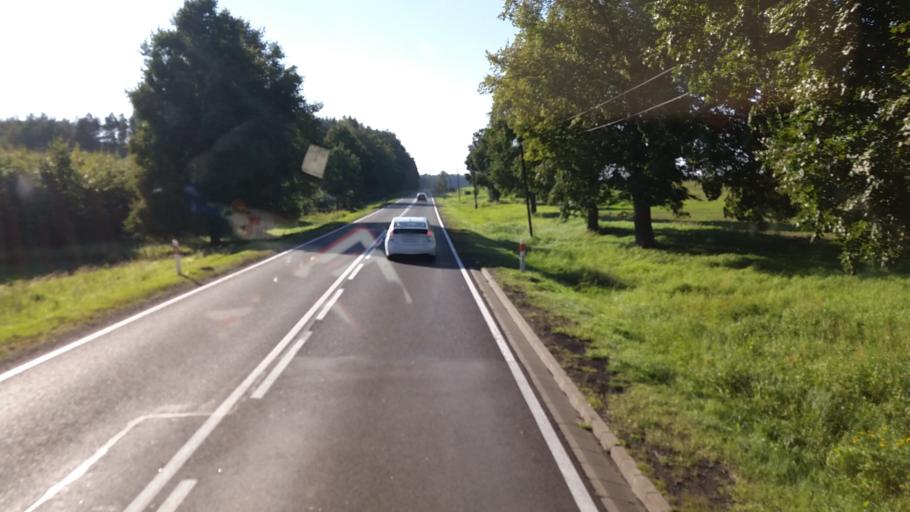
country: PL
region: West Pomeranian Voivodeship
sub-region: Powiat drawski
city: Kalisz Pomorski
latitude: 53.2965
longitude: 15.8313
